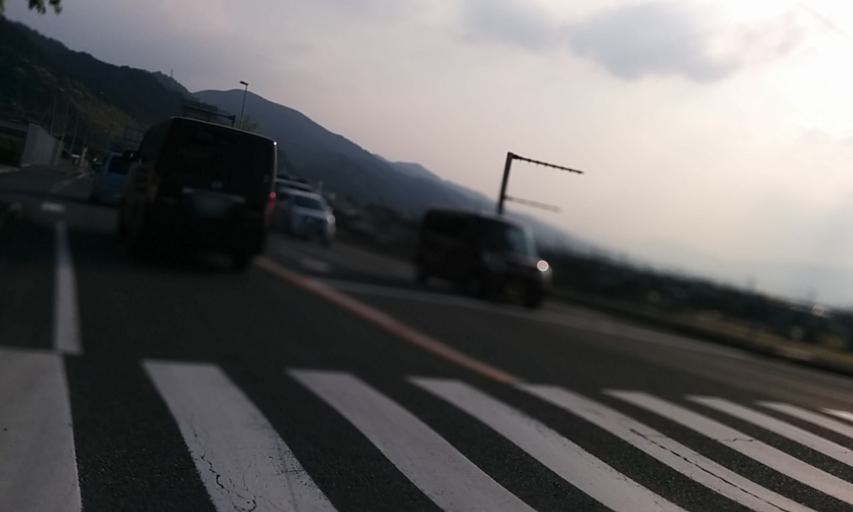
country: JP
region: Ehime
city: Saijo
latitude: 33.9023
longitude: 133.1833
